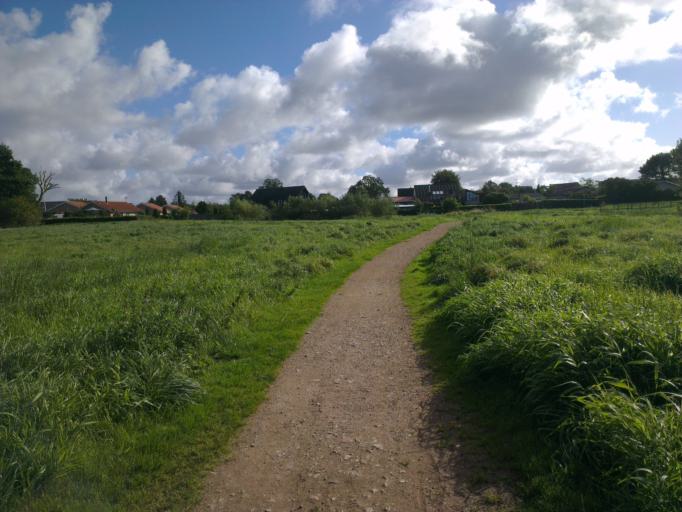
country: DK
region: Capital Region
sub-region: Frederikssund Kommune
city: Slangerup
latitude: 55.8429
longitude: 12.1679
